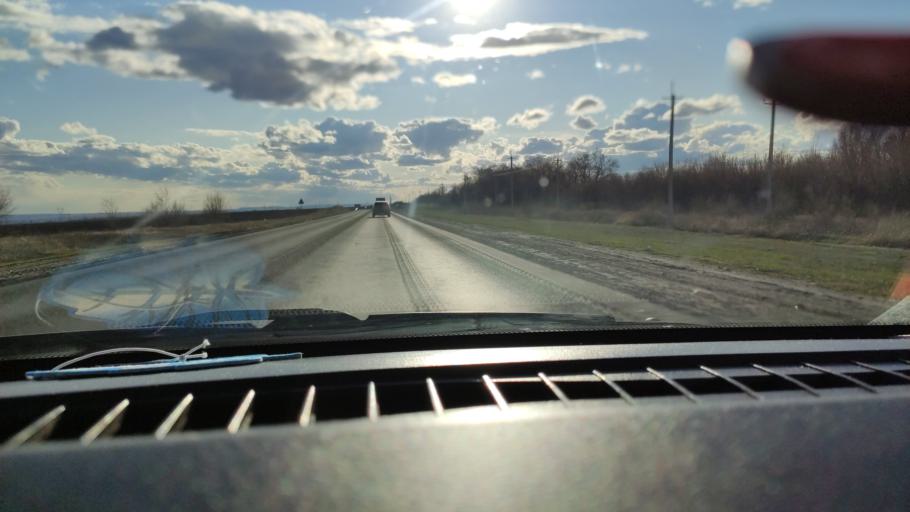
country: RU
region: Saratov
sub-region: Saratovskiy Rayon
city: Saratov
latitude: 51.7753
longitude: 46.0967
